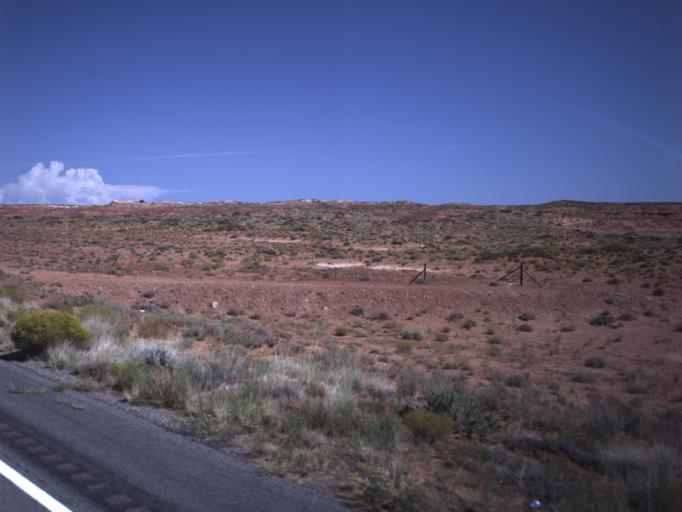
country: US
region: Utah
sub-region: San Juan County
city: Blanding
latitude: 37.0060
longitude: -109.6110
